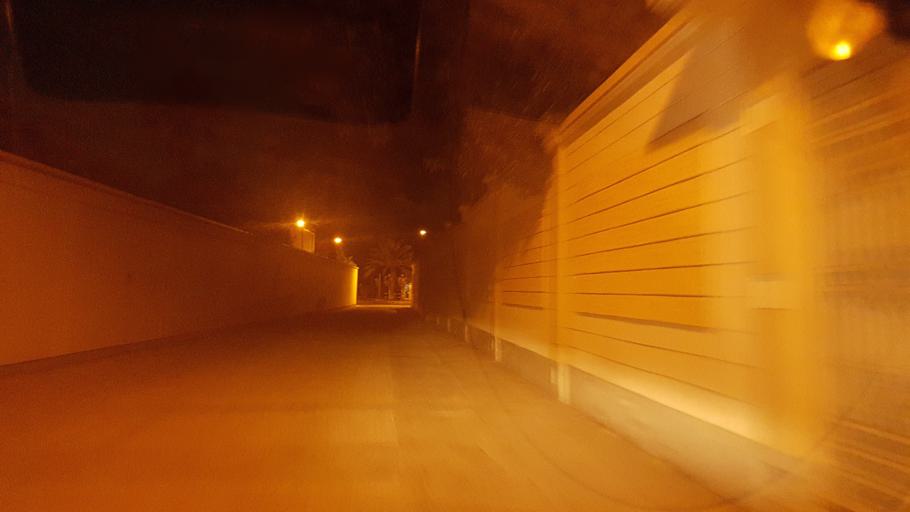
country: BH
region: Manama
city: Jidd Hafs
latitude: 26.2219
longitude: 50.4935
